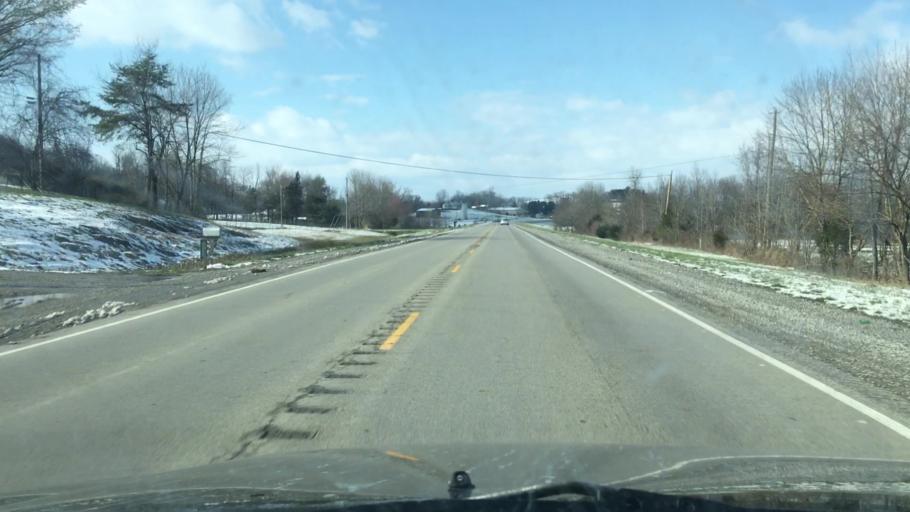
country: US
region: Kentucky
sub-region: Marion County
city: Lebanon
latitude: 37.5313
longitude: -85.3040
